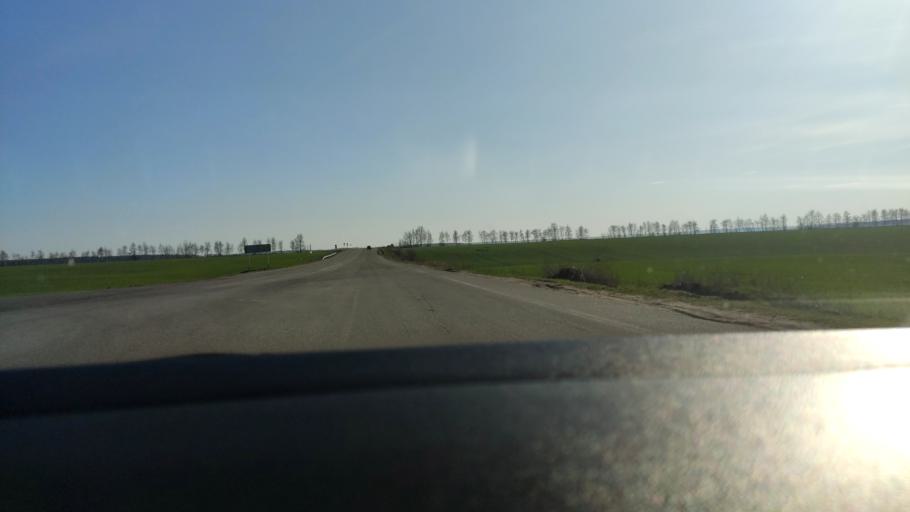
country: RU
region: Voronezj
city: Kolodeznyy
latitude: 51.3979
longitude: 39.2356
